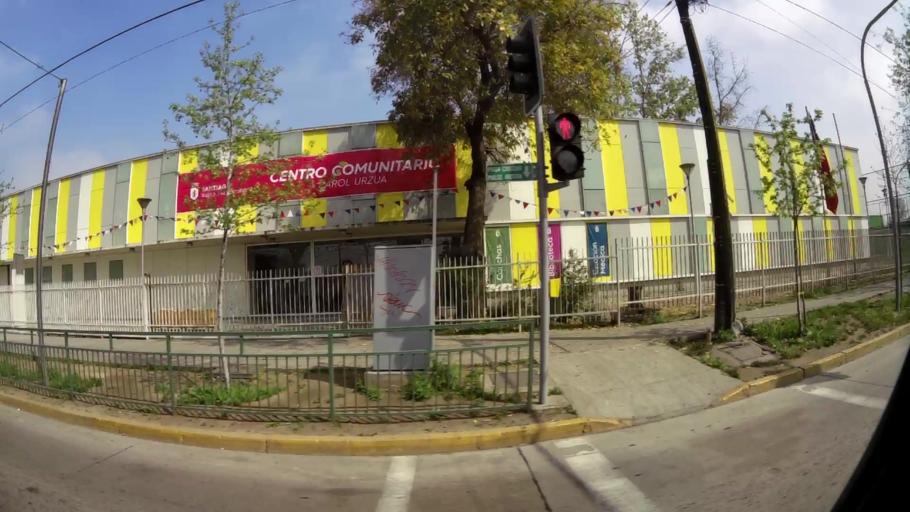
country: CL
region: Santiago Metropolitan
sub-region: Provincia de Santiago
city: Santiago
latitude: -33.4678
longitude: -70.6424
